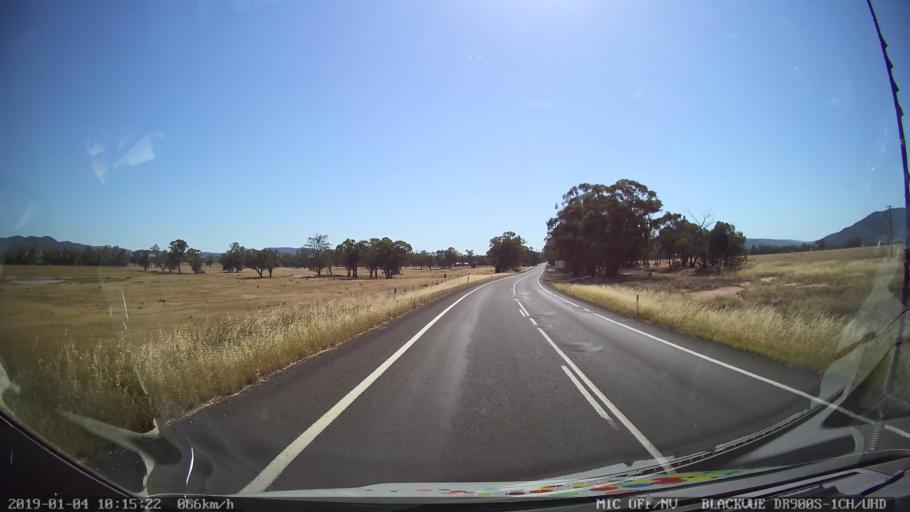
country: AU
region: New South Wales
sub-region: Cabonne
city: Canowindra
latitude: -33.3874
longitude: 148.4203
